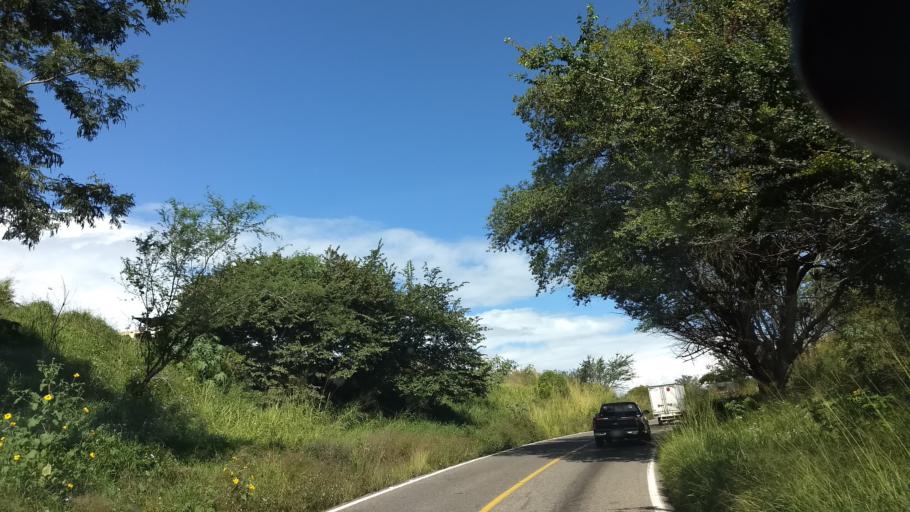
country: MX
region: Jalisco
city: Tuxpan
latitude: 19.5261
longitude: -103.4231
